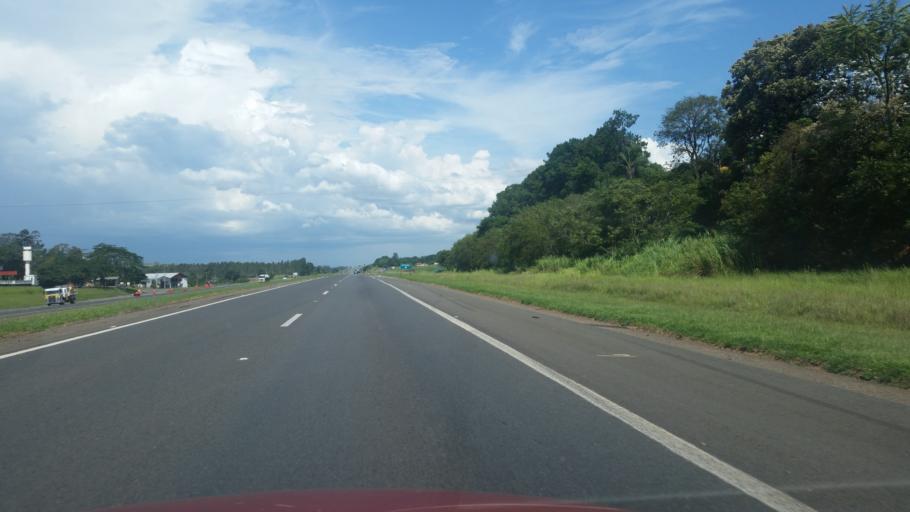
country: BR
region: Sao Paulo
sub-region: Tatui
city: Tatui
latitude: -23.2516
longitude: -47.9710
